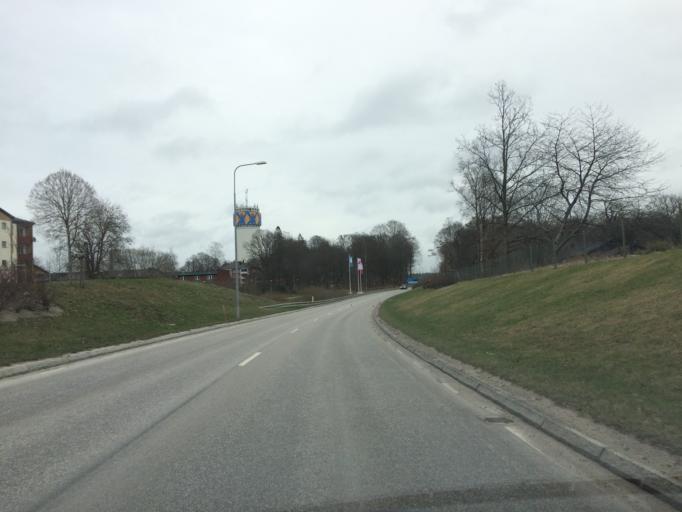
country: SE
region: Kronoberg
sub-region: Almhults Kommun
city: AElmhult
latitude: 56.5496
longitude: 14.1417
